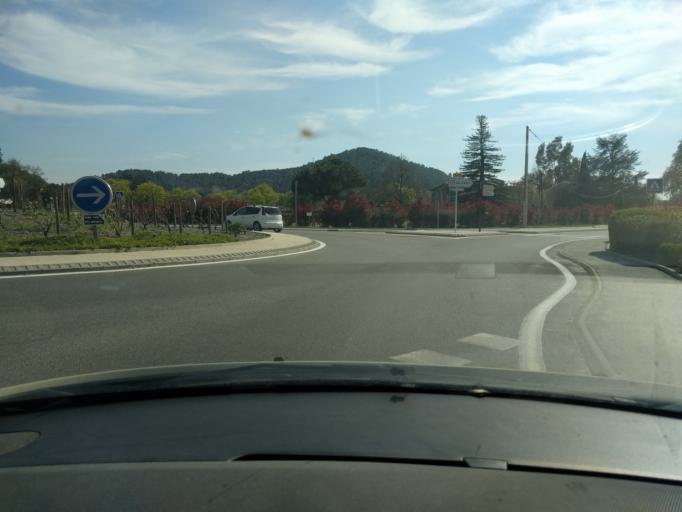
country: FR
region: Provence-Alpes-Cote d'Azur
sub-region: Departement du Var
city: La Crau
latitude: 43.1726
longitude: 6.1180
